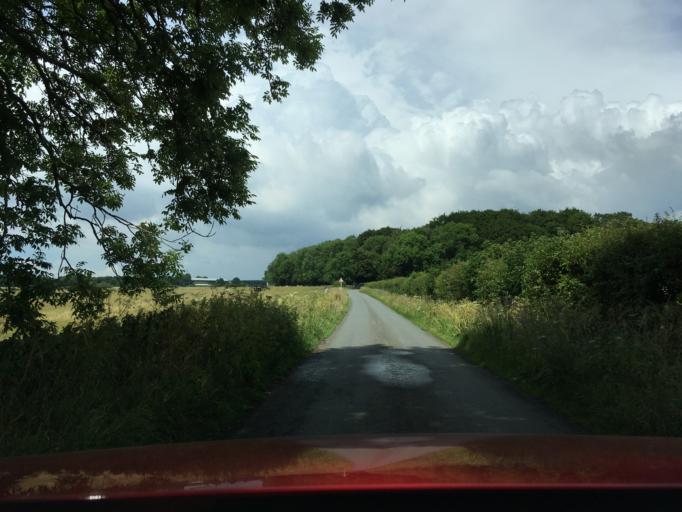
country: GB
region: England
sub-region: Gloucestershire
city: Chalford
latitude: 51.6941
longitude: -2.1260
